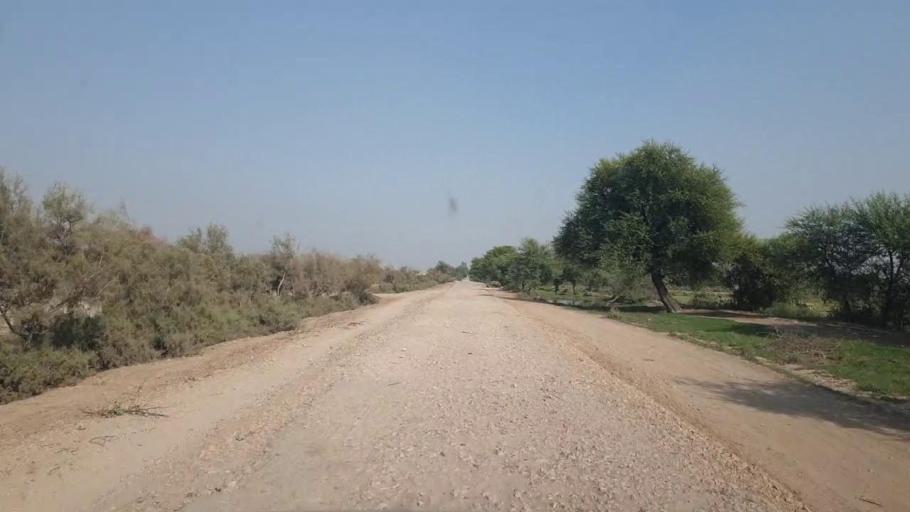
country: PK
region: Sindh
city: Sinjhoro
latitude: 26.0555
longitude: 68.8362
